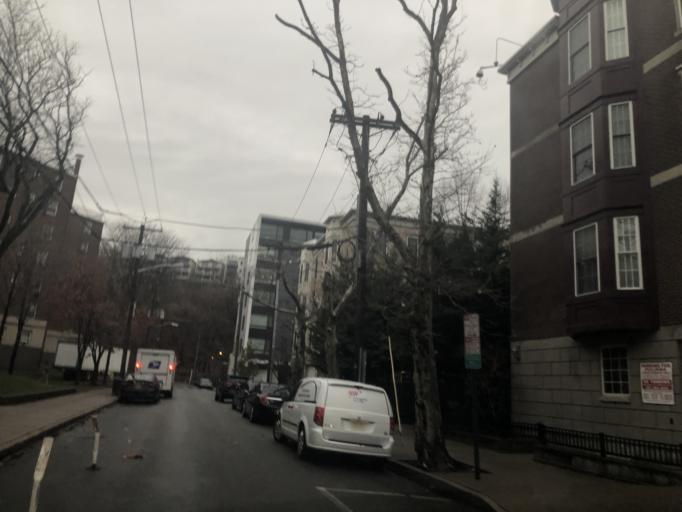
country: US
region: New Jersey
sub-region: Hudson County
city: Hoboken
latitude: 40.7453
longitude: -74.0394
